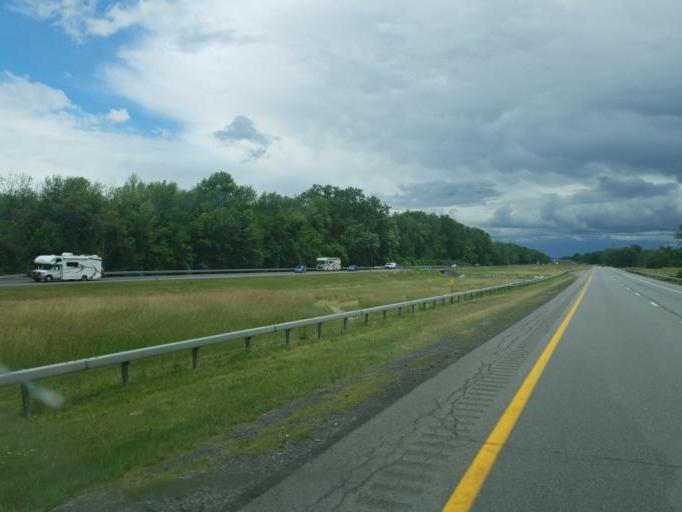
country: US
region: New York
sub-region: Ontario County
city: Clifton Springs
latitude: 42.9729
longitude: -77.1600
